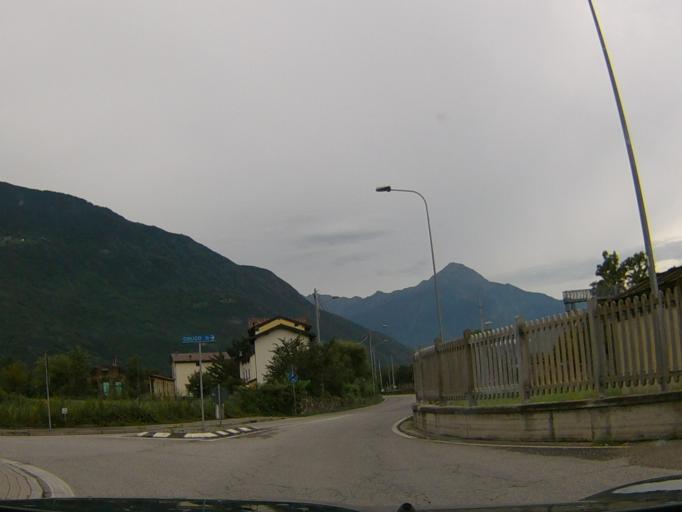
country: IT
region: Lombardy
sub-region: Provincia di Sondrio
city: Novate Mezzola
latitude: 46.2157
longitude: 9.4471
